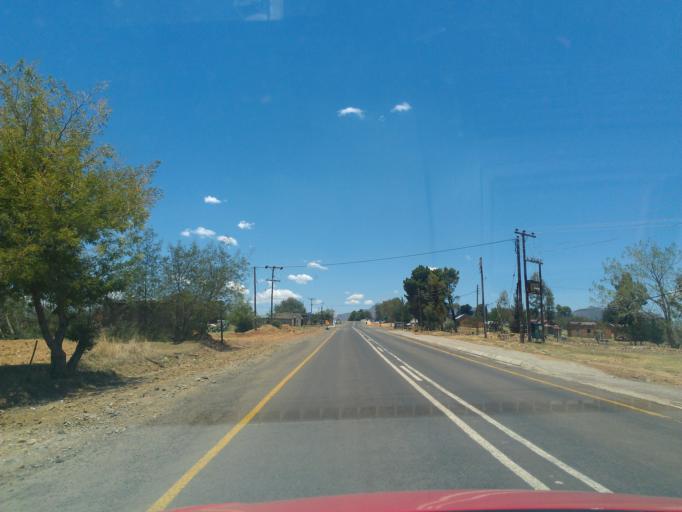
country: LS
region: Berea
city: Teyateyaneng
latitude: -29.1062
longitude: 27.9629
